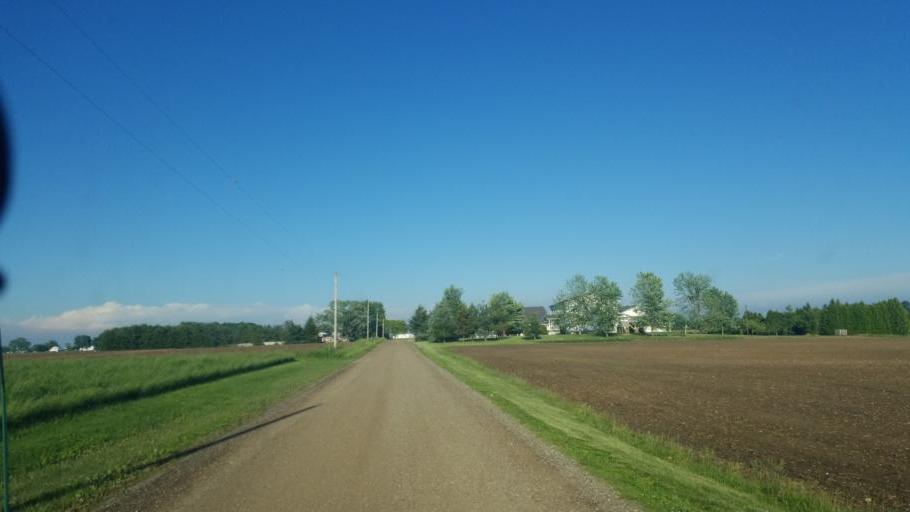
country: US
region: Indiana
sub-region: Marshall County
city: Bremen
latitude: 41.4099
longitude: -86.1035
